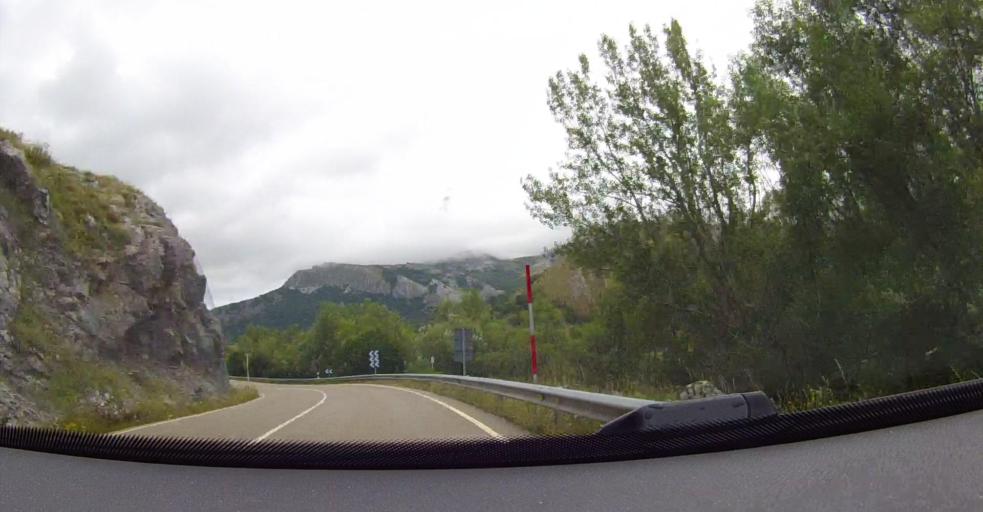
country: ES
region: Castille and Leon
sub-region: Provincia de Leon
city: Buron
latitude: 43.0276
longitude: -5.0643
